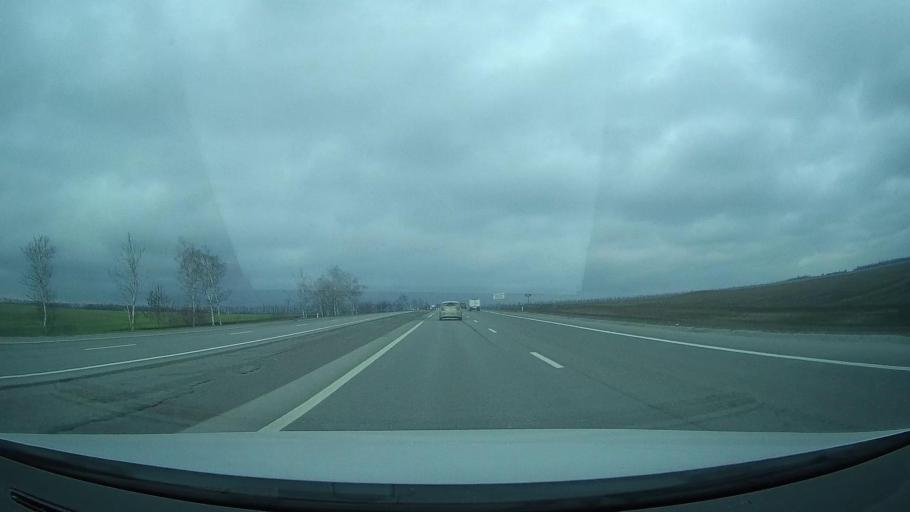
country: RU
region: Rostov
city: Grushevskaya
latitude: 47.4876
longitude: 39.9706
